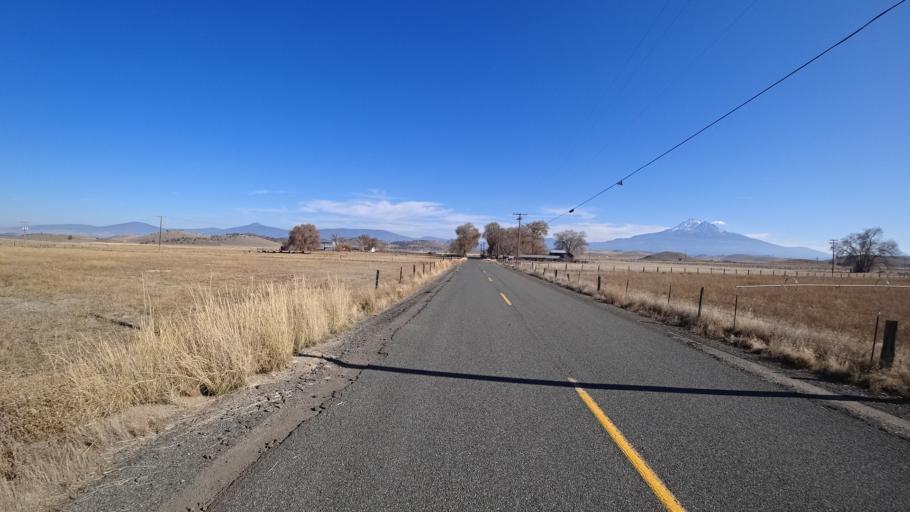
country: US
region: California
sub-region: Siskiyou County
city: Montague
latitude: 41.5746
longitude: -122.5289
